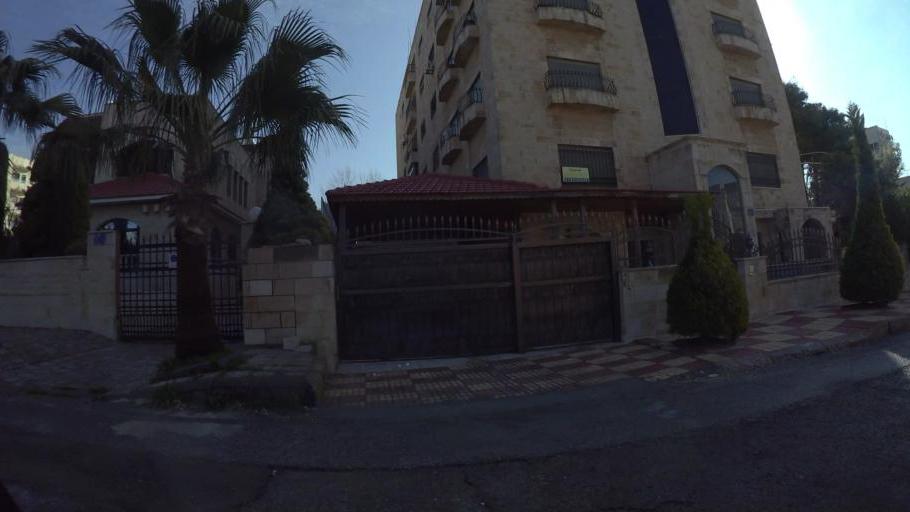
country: JO
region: Amman
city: Al Jubayhah
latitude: 32.0058
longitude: 35.8509
